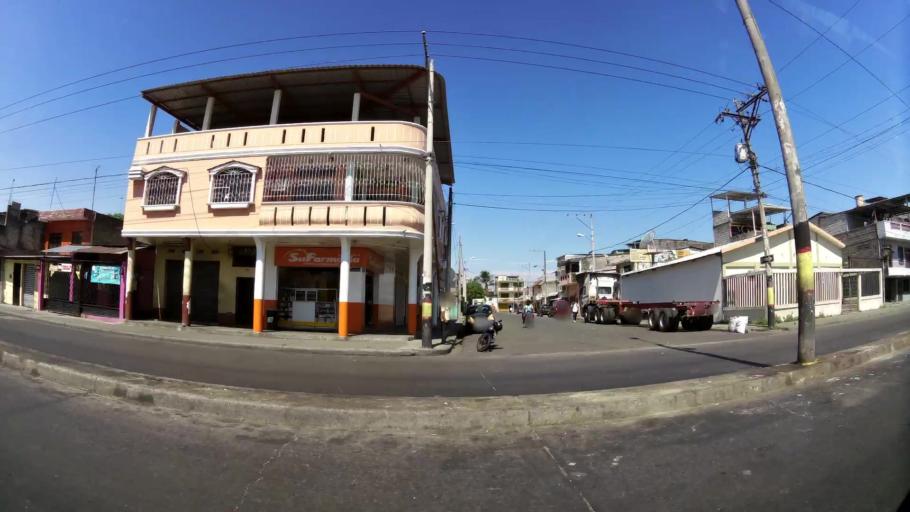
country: EC
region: Guayas
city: Guayaquil
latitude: -2.2244
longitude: -79.9425
